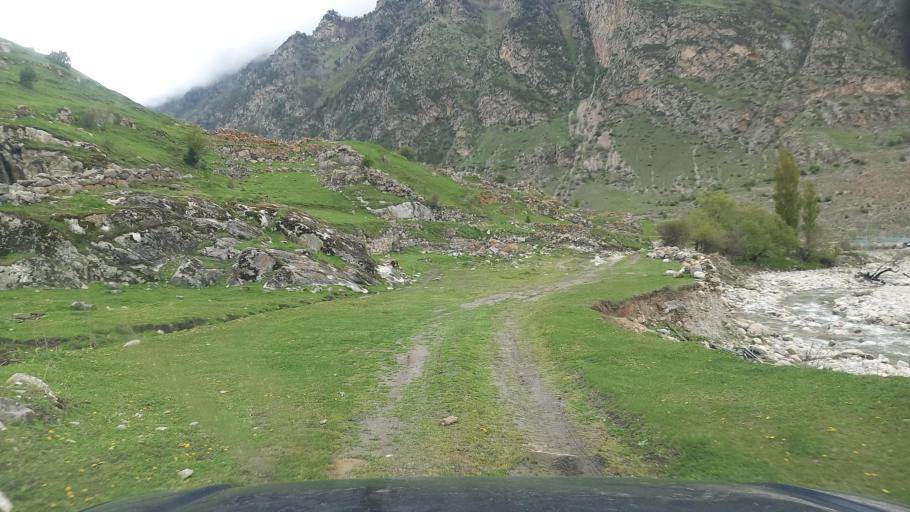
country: RU
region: Kabardino-Balkariya
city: Verkhnyaya Balkariya
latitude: 43.1023
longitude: 43.4375
